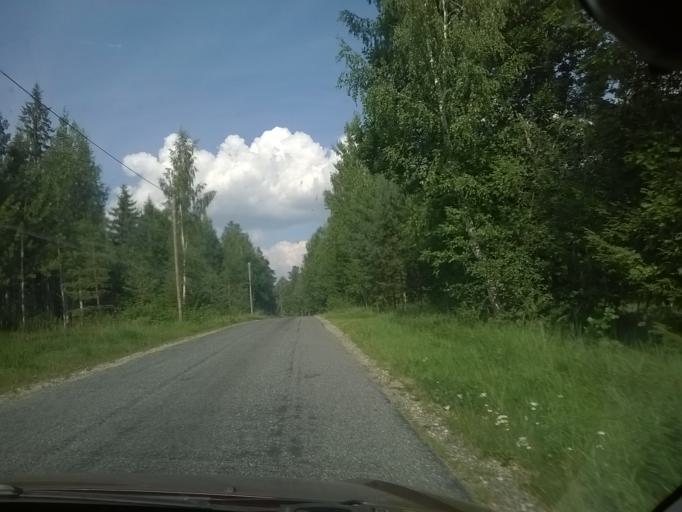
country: EE
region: Tartu
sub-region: Puhja vald
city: Puhja
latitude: 58.2407
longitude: 26.1743
